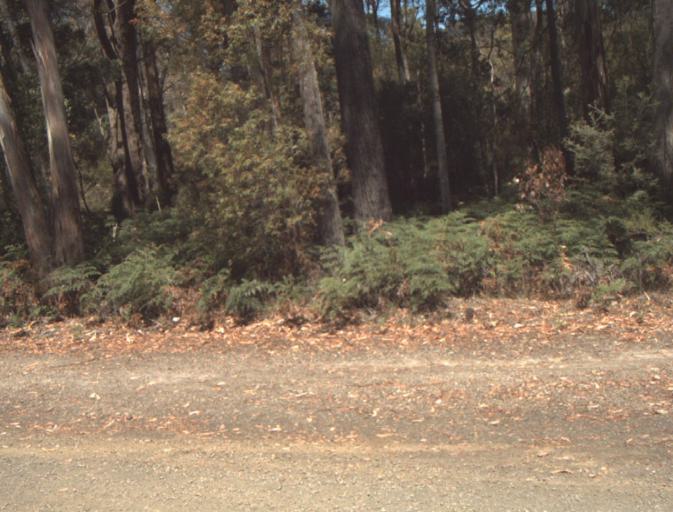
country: AU
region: Tasmania
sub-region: Launceston
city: Newstead
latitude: -41.3488
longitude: 147.3765
